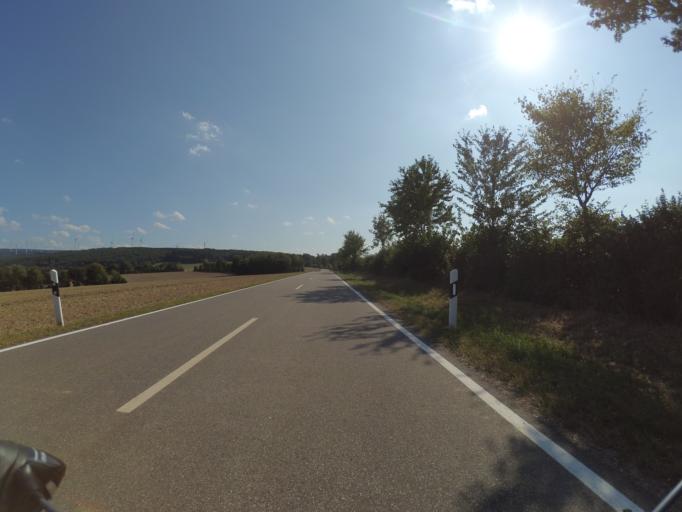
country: DE
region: Rheinland-Pfalz
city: Wintrich
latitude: 49.8727
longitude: 6.9628
